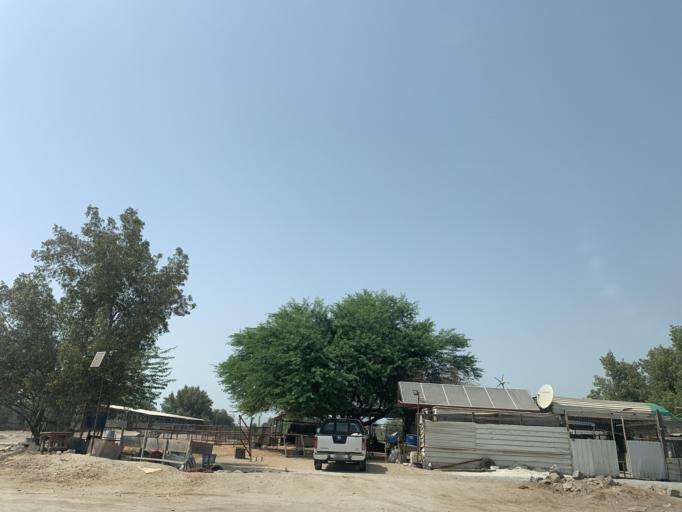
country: BH
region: Manama
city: Jidd Hafs
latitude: 26.2124
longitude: 50.5167
